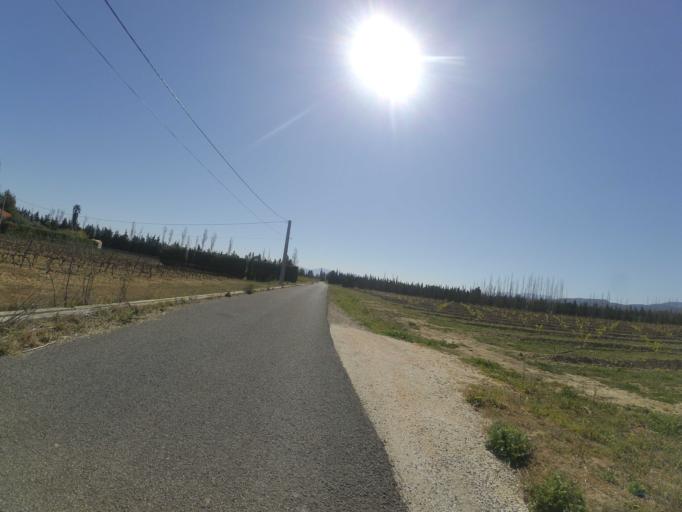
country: FR
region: Languedoc-Roussillon
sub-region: Departement des Pyrenees-Orientales
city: Corneilla-la-Riviere
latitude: 42.6791
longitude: 2.7236
